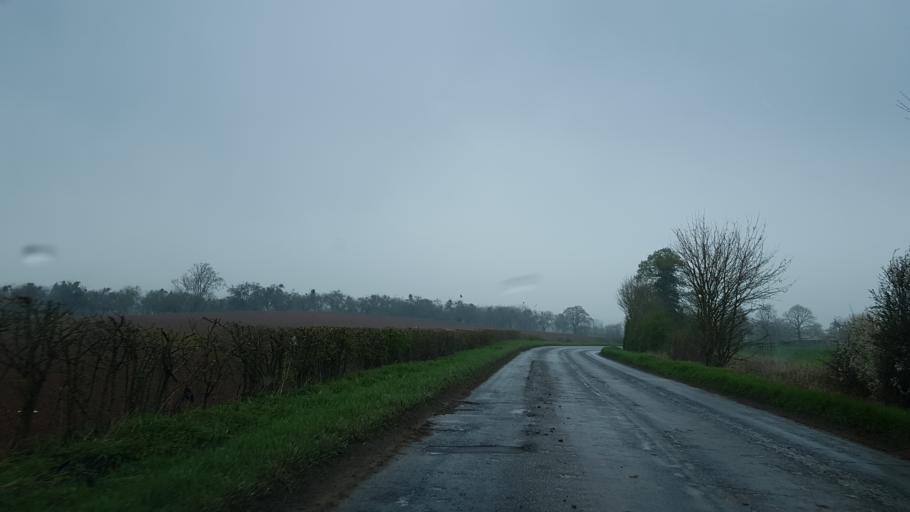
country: GB
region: England
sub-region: Herefordshire
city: Ledbury
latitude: 52.0767
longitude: -2.4567
